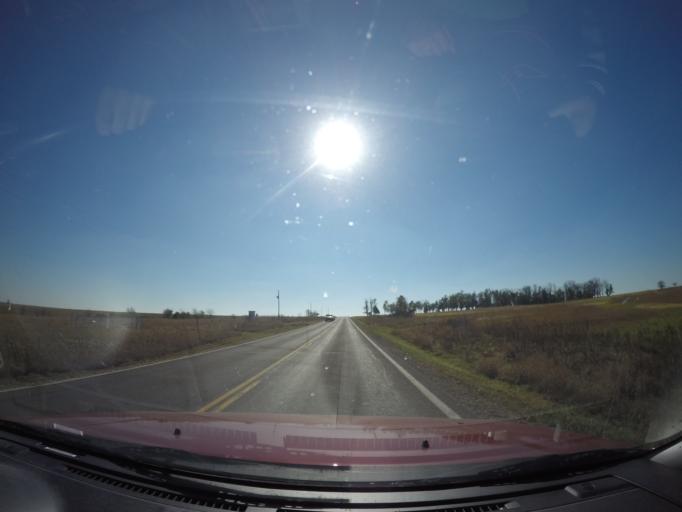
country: US
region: Kansas
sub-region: Morris County
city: Council Grove
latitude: 38.7674
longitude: -96.5012
